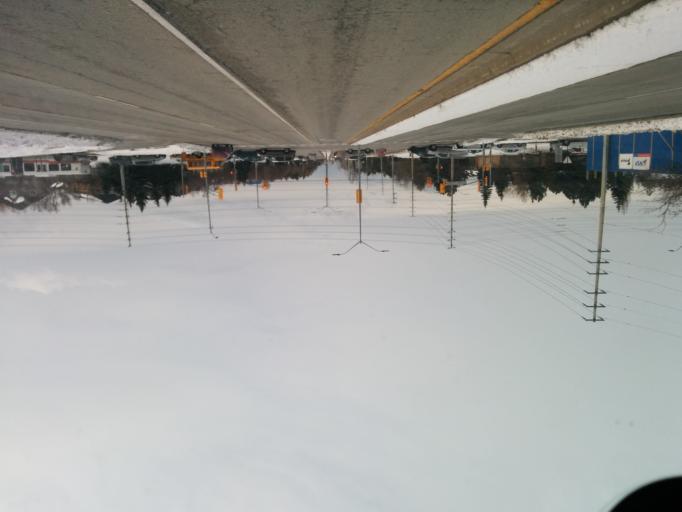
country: CA
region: Ontario
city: Mississauga
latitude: 43.5374
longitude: -79.6670
